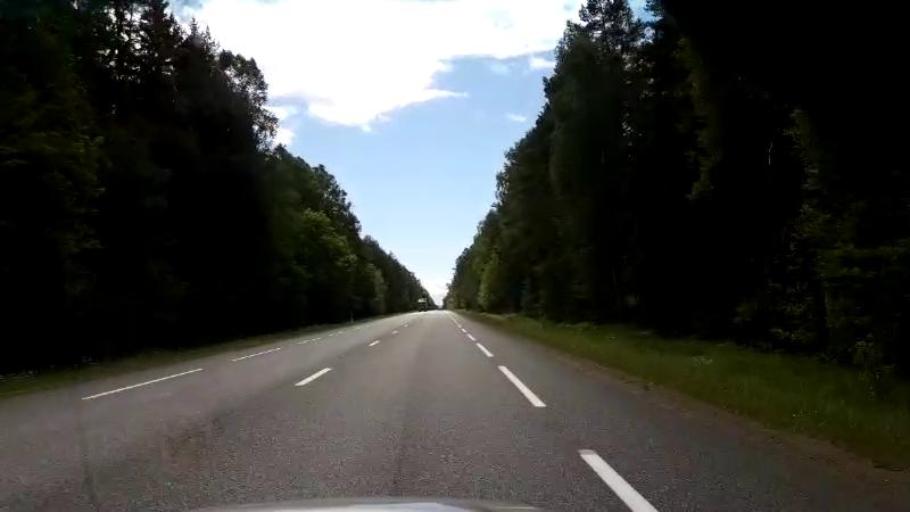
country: LV
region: Saulkrastu
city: Saulkrasti
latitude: 57.4822
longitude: 24.4331
